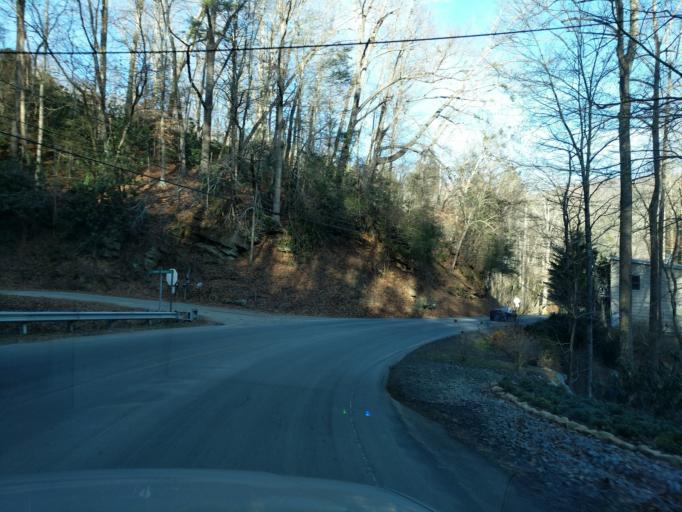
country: US
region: North Carolina
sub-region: Henderson County
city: Edneyville
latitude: 35.4377
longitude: -82.2995
